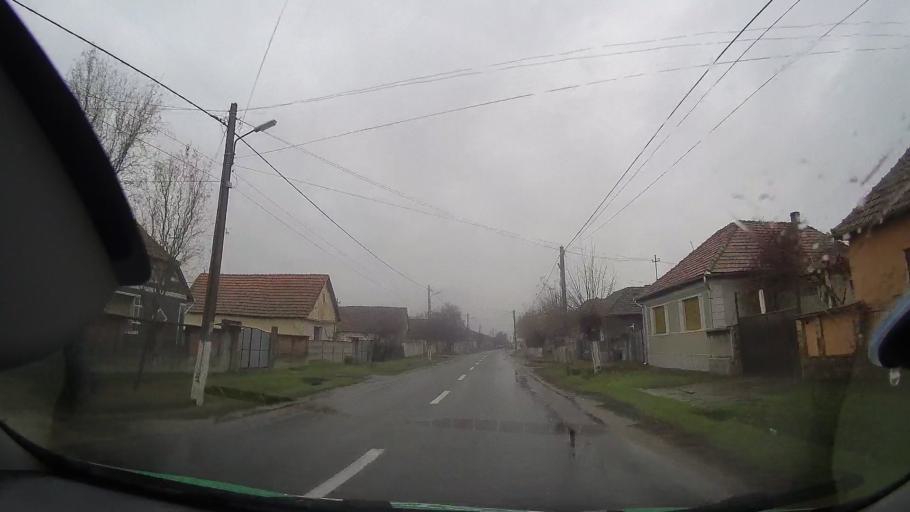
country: RO
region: Bihor
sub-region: Comuna Tinca
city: Gurbediu
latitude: 46.7918
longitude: 21.8588
